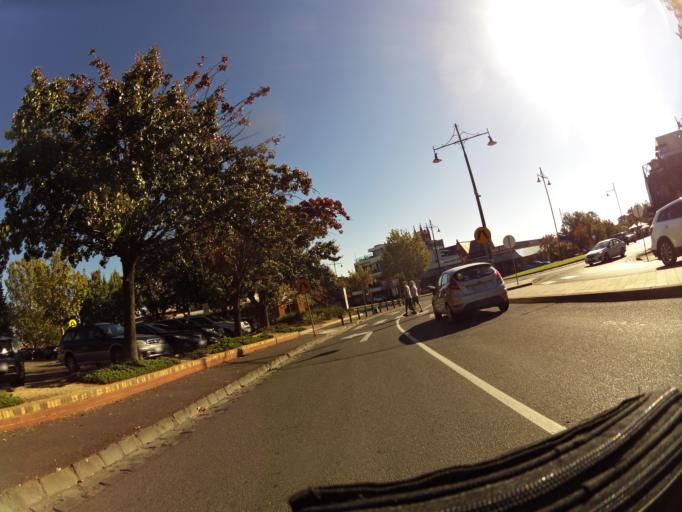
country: AU
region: Victoria
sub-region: Greater Bendigo
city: Bendigo
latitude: -36.7638
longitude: 144.2826
